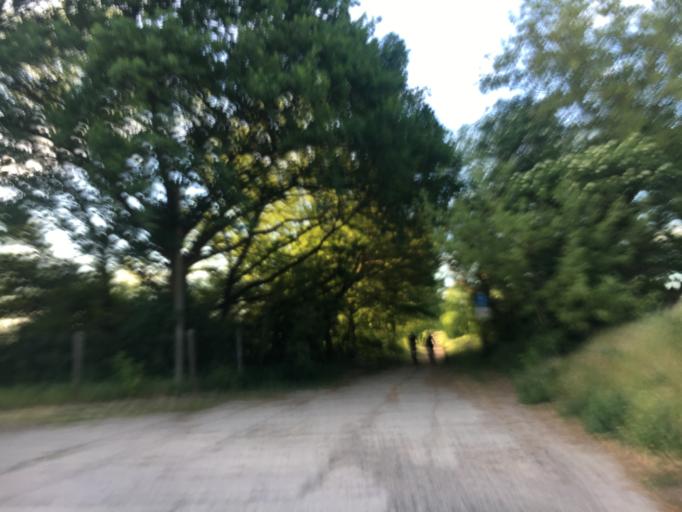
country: DE
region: Brandenburg
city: Potsdam
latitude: 52.4259
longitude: 13.0251
